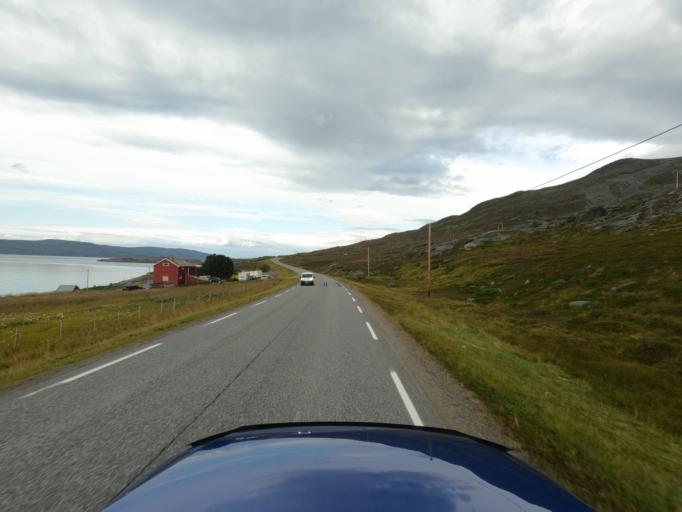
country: NO
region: Finnmark Fylke
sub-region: Hammerfest
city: Rypefjord
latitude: 70.5519
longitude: 23.7225
